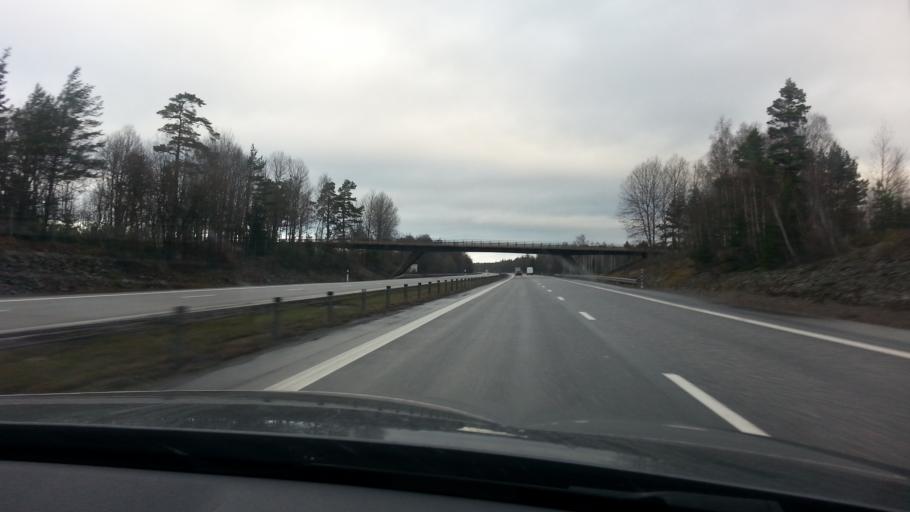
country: SE
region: Joenkoeping
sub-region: Jonkopings Kommun
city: Asa
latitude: 58.0834
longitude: 14.5419
